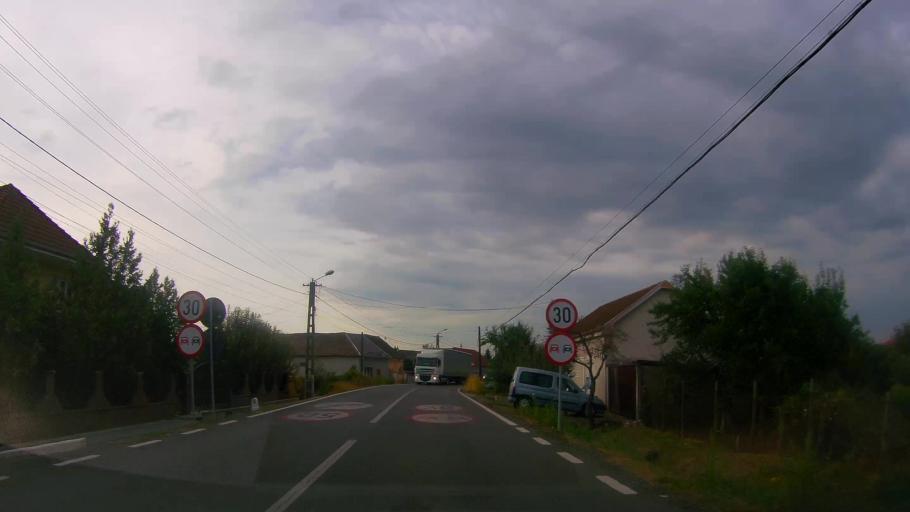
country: RO
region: Satu Mare
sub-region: Comuna Halmeu
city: Halmeu
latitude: 47.9788
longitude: 23.0100
